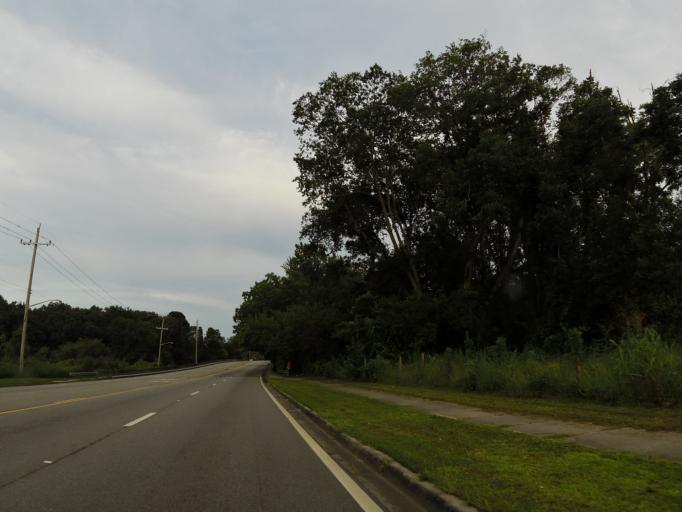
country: US
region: Florida
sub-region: Duval County
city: Jacksonville
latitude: 30.3895
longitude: -81.7225
